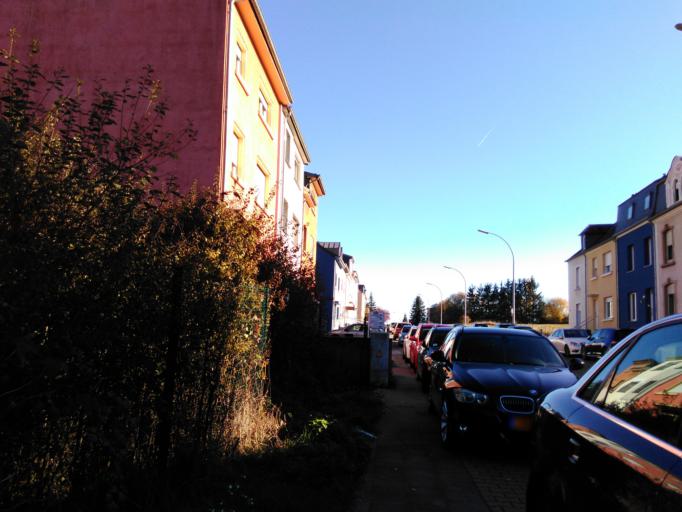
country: LU
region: Luxembourg
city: Belvaux
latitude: 49.5038
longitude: 5.9313
